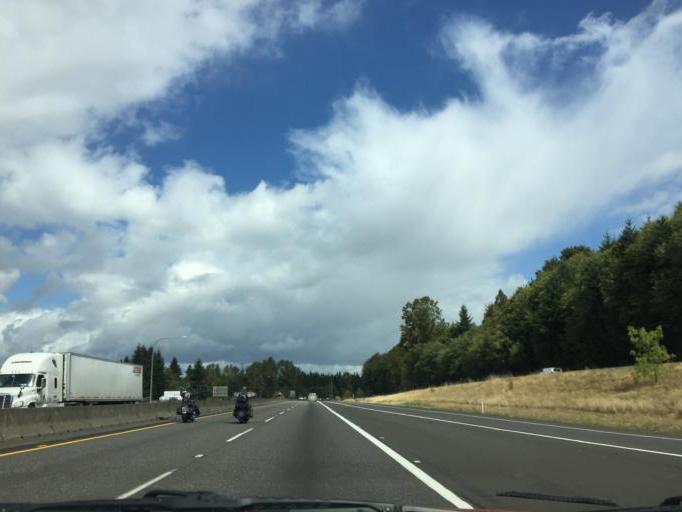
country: US
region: Washington
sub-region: Lewis County
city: Winlock
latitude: 46.3936
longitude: -122.9009
